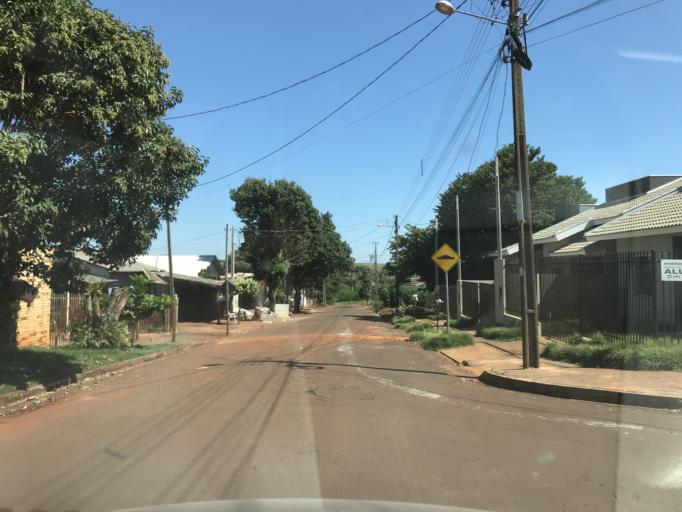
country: BR
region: Parana
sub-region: Palotina
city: Palotina
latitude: -24.2974
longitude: -53.8452
